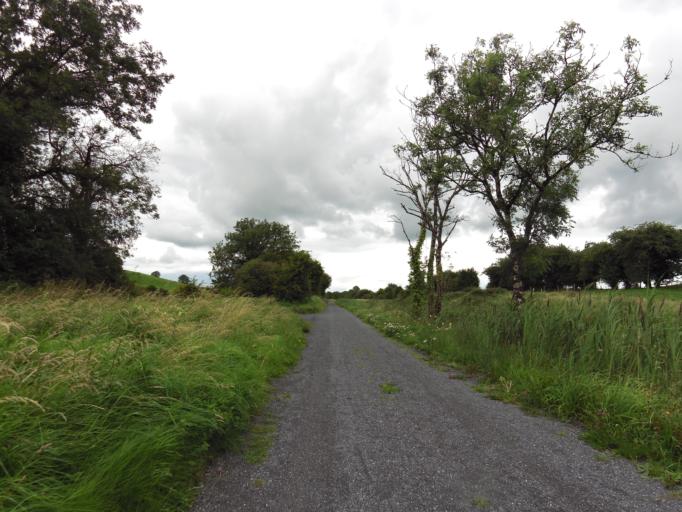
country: IE
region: Leinster
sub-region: An Iarmhi
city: An Muileann gCearr
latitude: 53.5311
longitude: -7.4615
